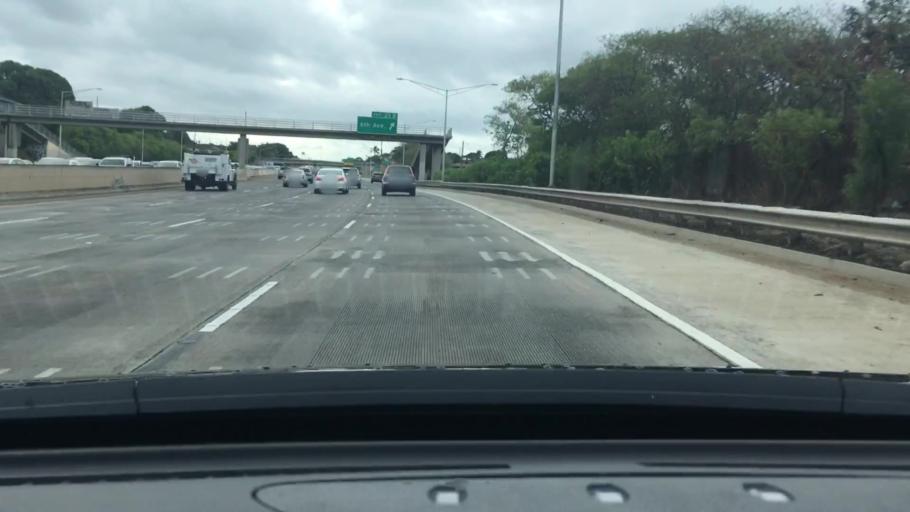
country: US
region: Hawaii
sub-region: Honolulu County
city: Honolulu
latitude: 21.2855
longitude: -157.8107
